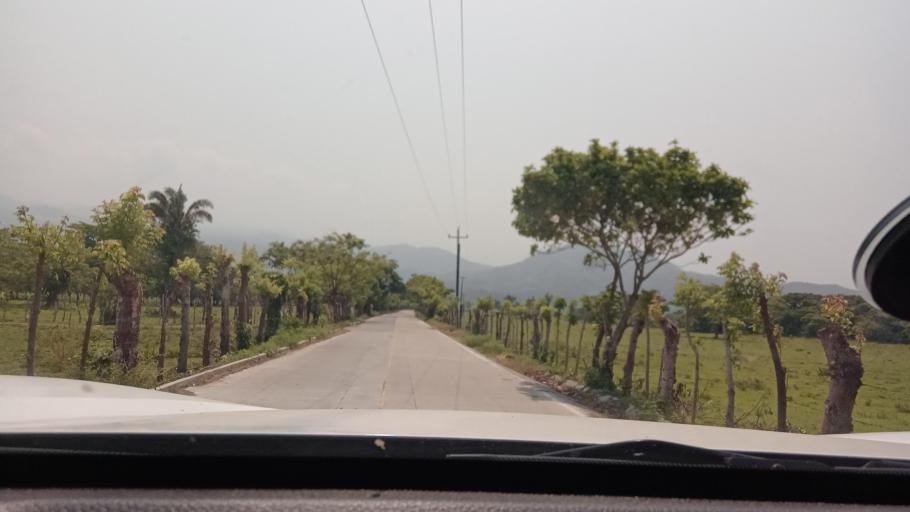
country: MX
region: Veracruz
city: Catemaco
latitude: 18.5621
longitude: -95.0424
